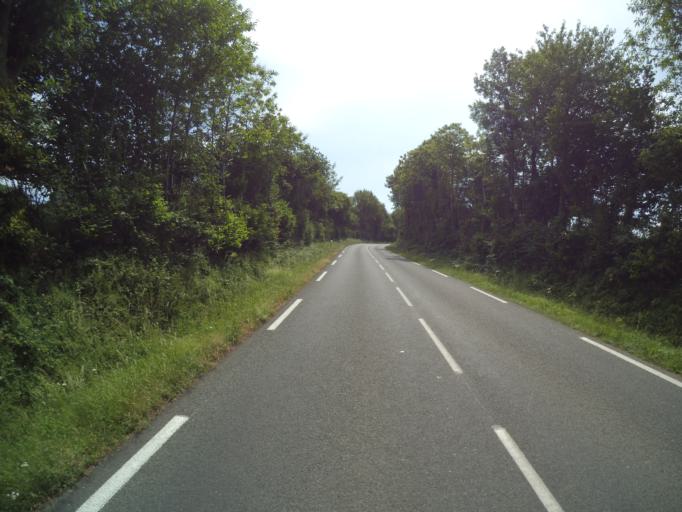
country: FR
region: Pays de la Loire
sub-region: Departement de la Vendee
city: Les Epesses
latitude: 46.8481
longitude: -0.9269
